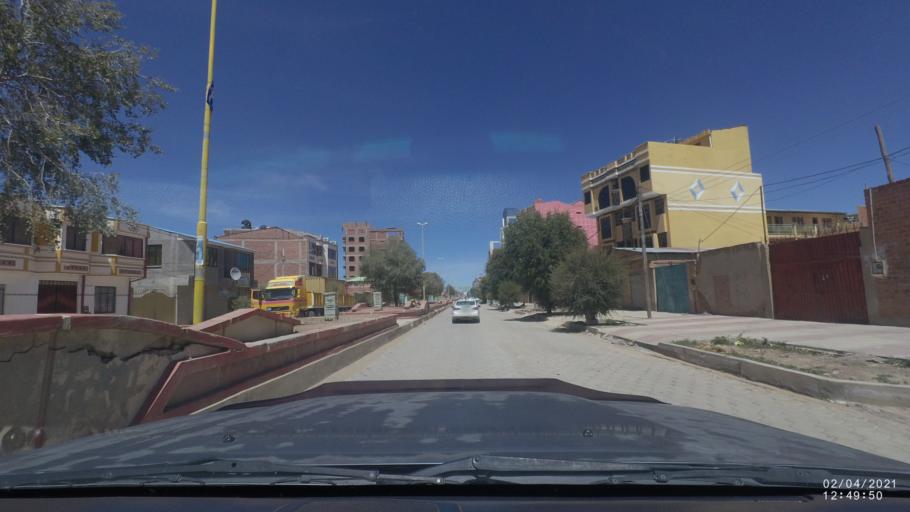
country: BO
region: Oruro
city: Oruro
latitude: -17.9742
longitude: -67.1382
